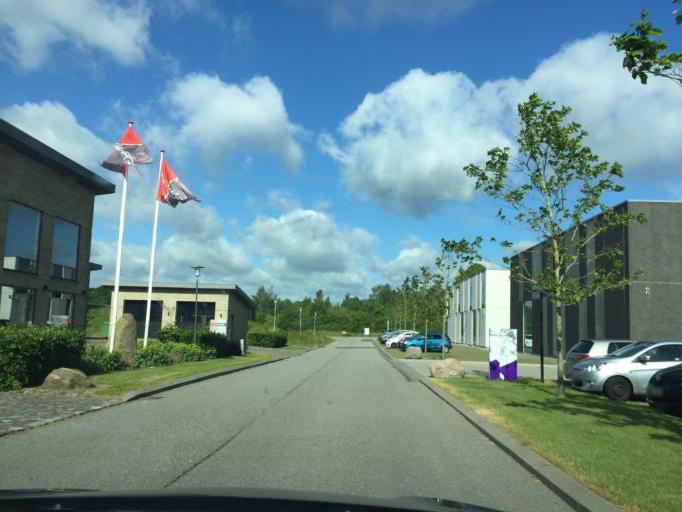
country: DK
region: South Denmark
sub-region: Odense Kommune
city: Odense
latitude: 55.3704
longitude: 10.3998
